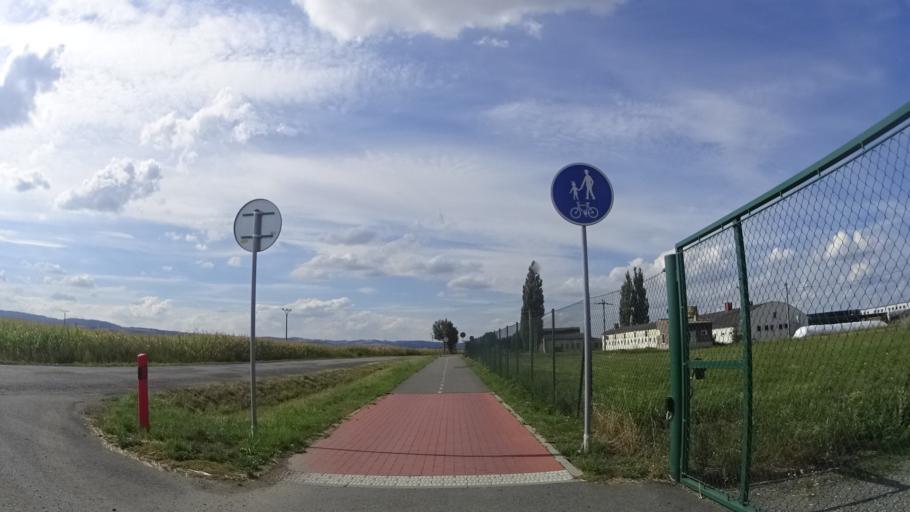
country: CZ
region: Olomoucky
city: Moravicany
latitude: 49.7600
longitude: 16.9533
